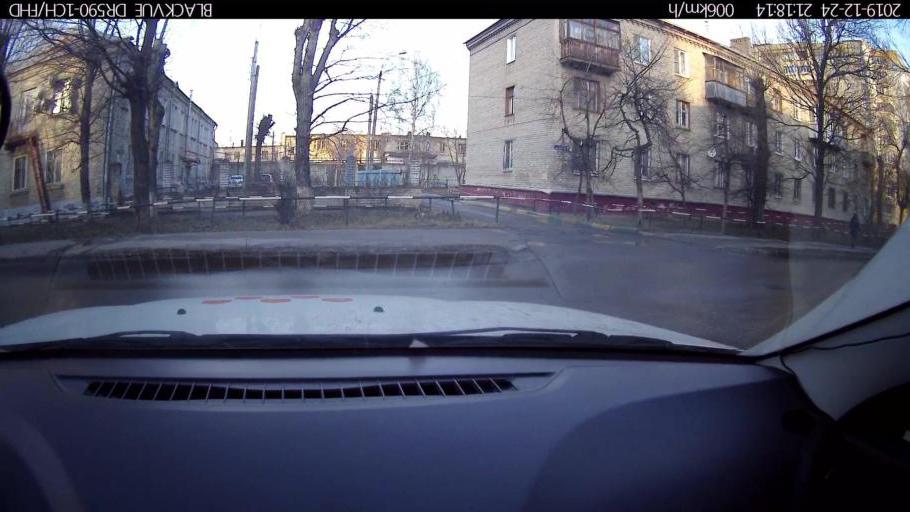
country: RU
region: Nizjnij Novgorod
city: Gorbatovka
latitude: 56.2652
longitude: 43.8776
